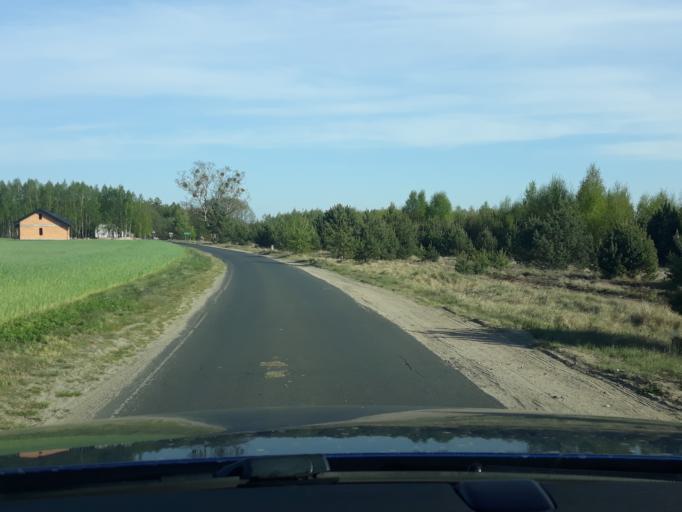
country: PL
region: Pomeranian Voivodeship
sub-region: Powiat czluchowski
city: Przechlewo
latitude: 53.8783
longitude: 17.3232
